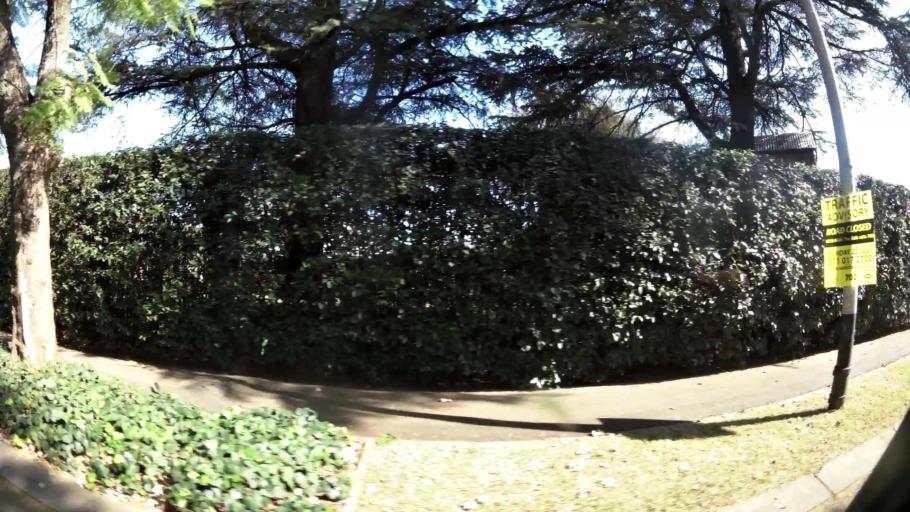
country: ZA
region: Gauteng
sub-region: City of Johannesburg Metropolitan Municipality
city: Johannesburg
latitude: -26.1526
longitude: 28.0114
